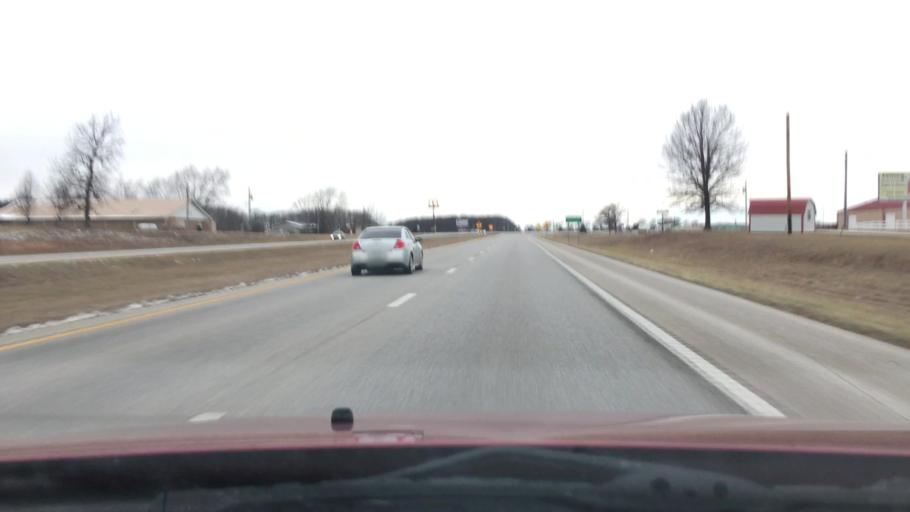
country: US
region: Missouri
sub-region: Webster County
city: Seymour
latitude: 37.1565
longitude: -92.7806
